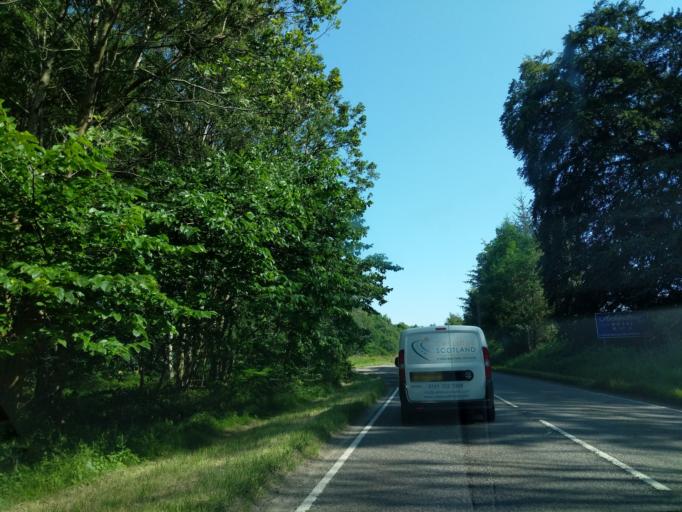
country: GB
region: Scotland
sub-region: Moray
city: Rothes
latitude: 57.5062
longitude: -3.1977
